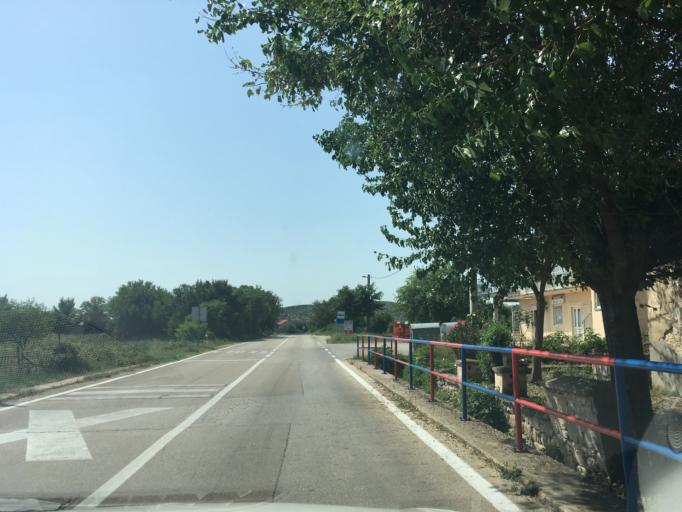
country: HR
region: Zadarska
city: Benkovac
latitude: 43.9618
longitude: 15.7655
